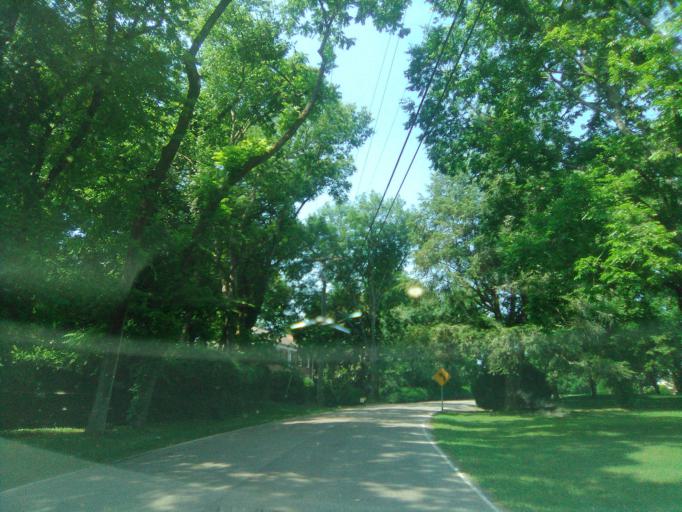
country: US
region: Tennessee
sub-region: Davidson County
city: Belle Meade
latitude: 36.1196
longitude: -86.8505
